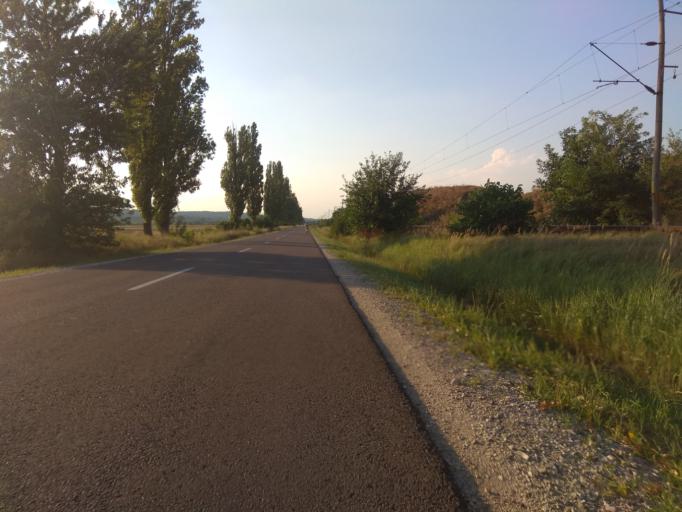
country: HU
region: Borsod-Abauj-Zemplen
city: Nyekladhaza
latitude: 47.9777
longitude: 20.8471
